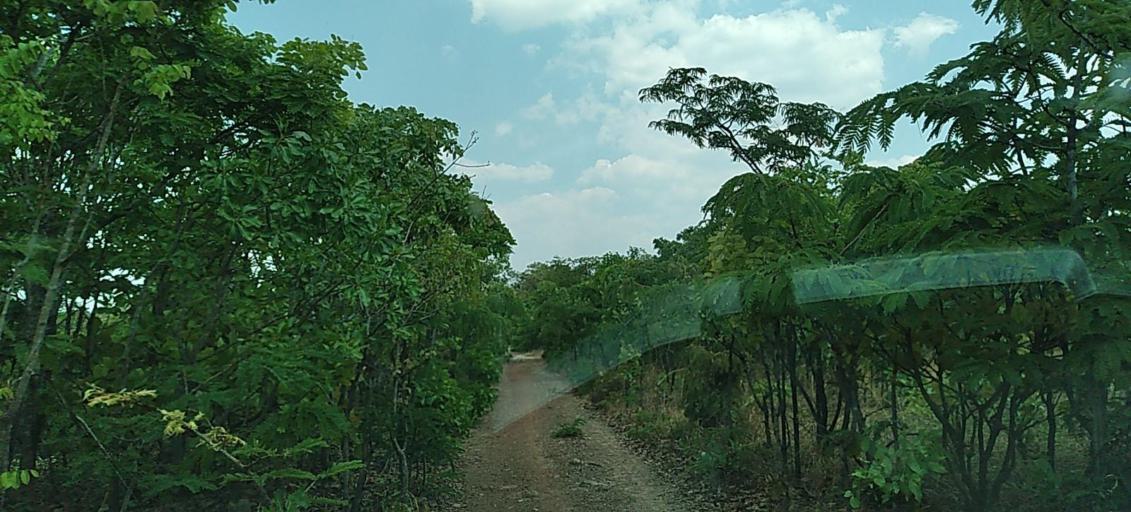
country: CD
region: Katanga
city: Kipushi
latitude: -12.0065
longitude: 27.4278
